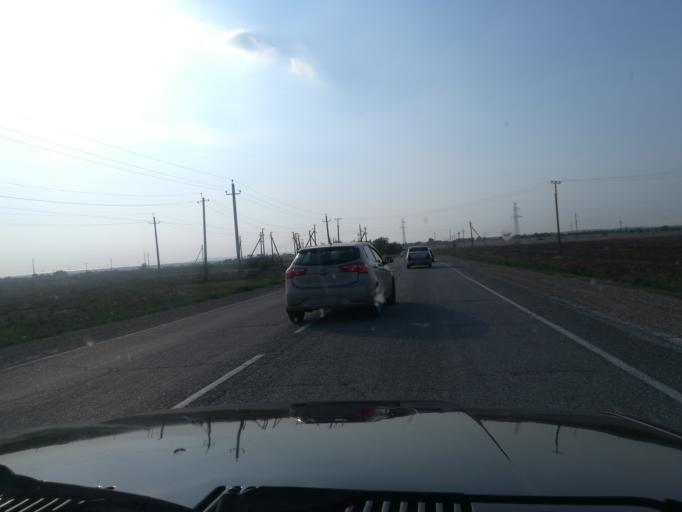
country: RU
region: Krasnodarskiy
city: Yurovka
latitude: 45.1014
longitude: 37.4275
